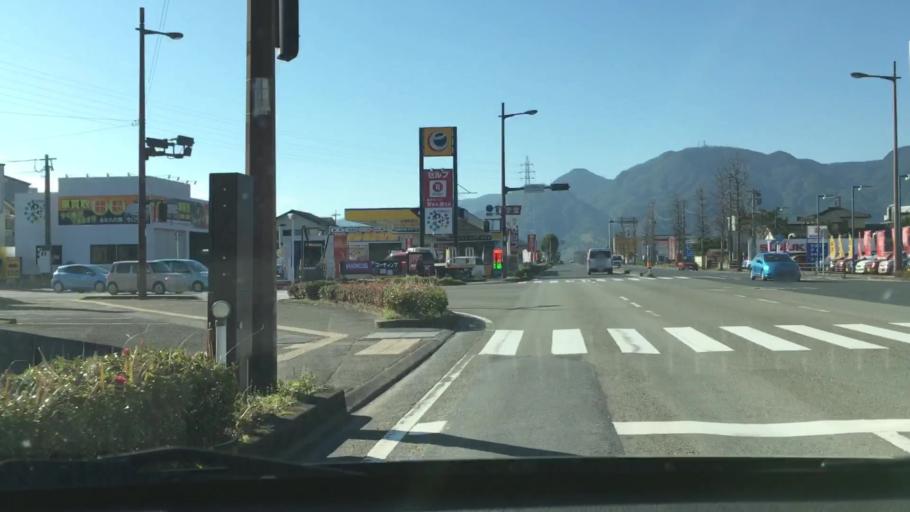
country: JP
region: Kagoshima
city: Kajiki
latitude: 31.7262
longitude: 130.6242
